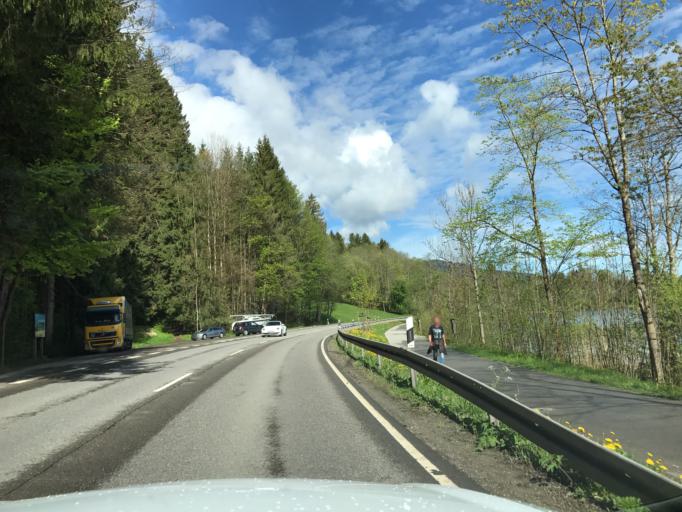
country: DE
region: Bavaria
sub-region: Upper Bavaria
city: Tegernsee
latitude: 47.6926
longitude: 11.7363
